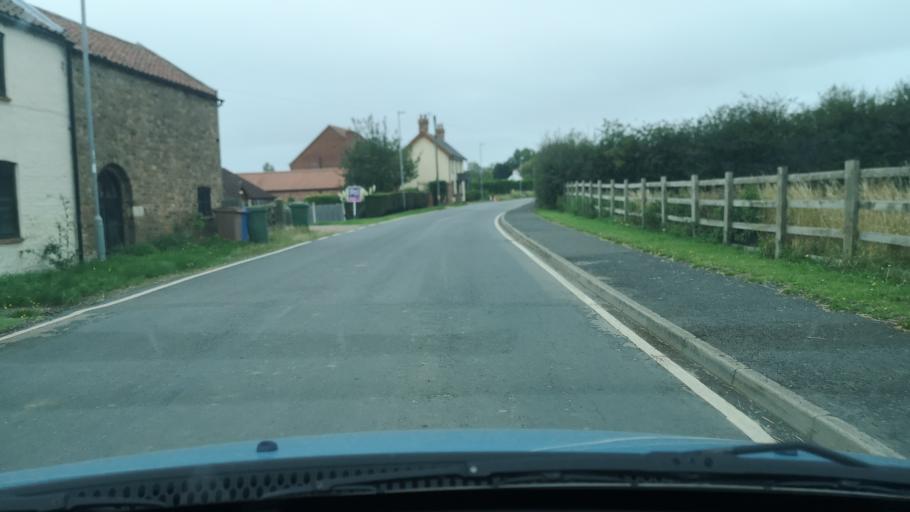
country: GB
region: England
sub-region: East Riding of Yorkshire
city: Laxton
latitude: 53.6967
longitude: -0.7593
